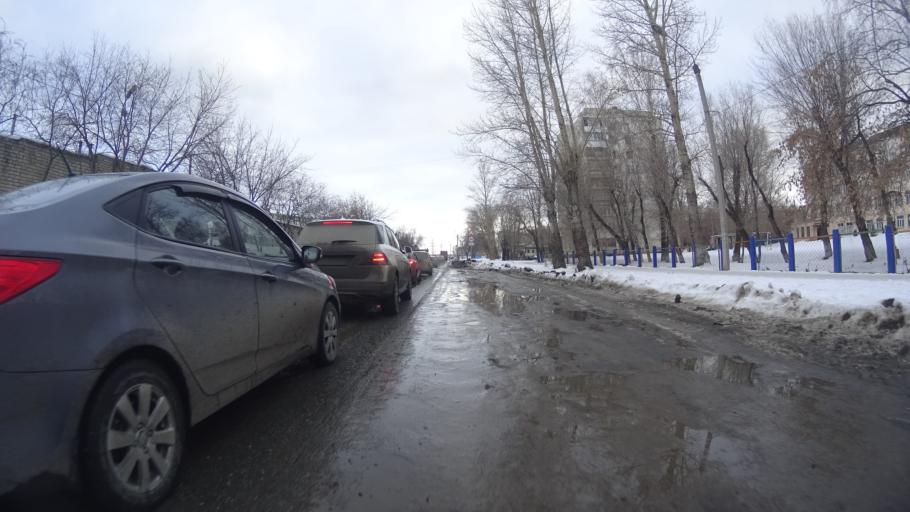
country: RU
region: Chelyabinsk
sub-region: Gorod Chelyabinsk
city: Chelyabinsk
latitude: 55.1416
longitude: 61.4012
